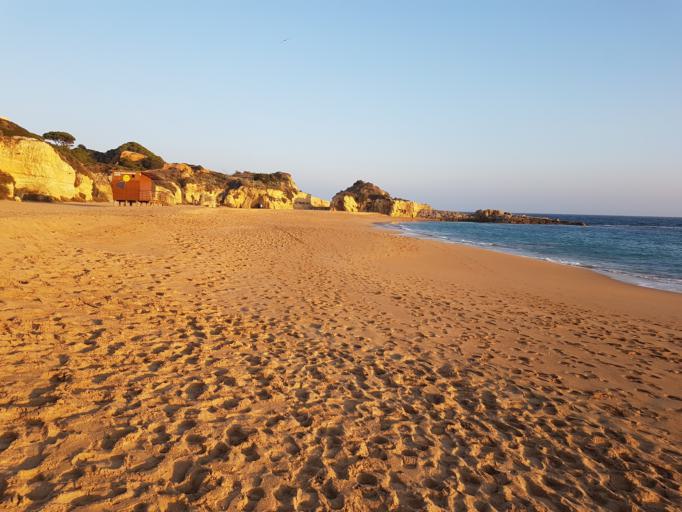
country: PT
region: Faro
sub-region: Albufeira
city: Albufeira
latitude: 37.0835
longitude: -8.2360
